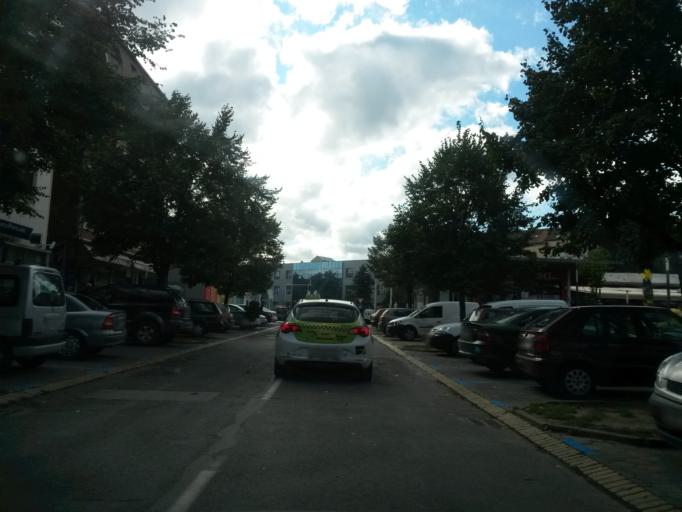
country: HR
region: Osjecko-Baranjska
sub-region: Grad Osijek
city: Osijek
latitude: 45.5558
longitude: 18.7199
